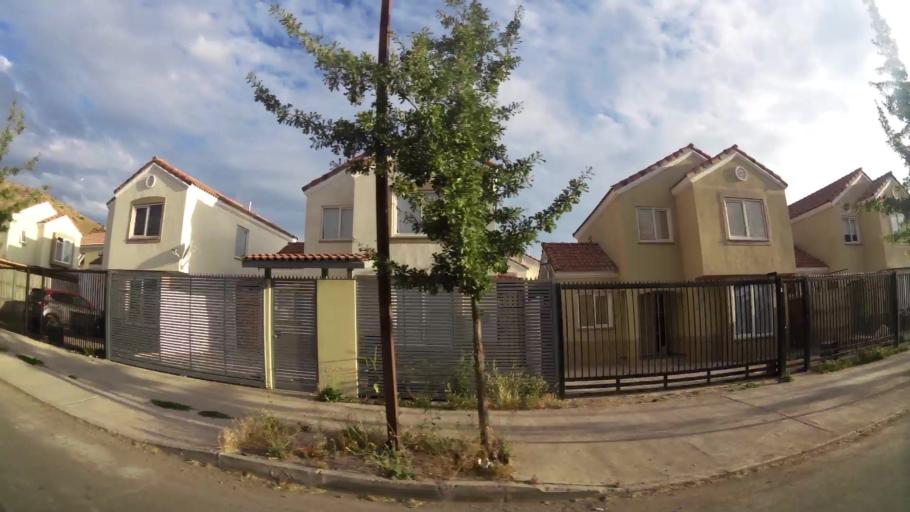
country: CL
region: Santiago Metropolitan
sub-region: Provincia de Maipo
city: San Bernardo
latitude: -33.6276
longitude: -70.6801
